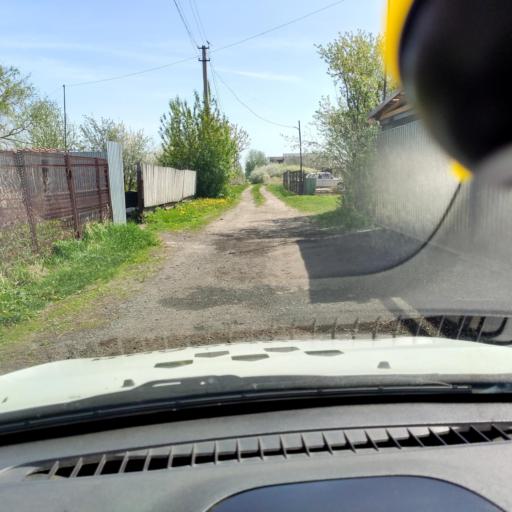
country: RU
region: Samara
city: Tol'yatti
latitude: 53.6677
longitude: 49.3632
